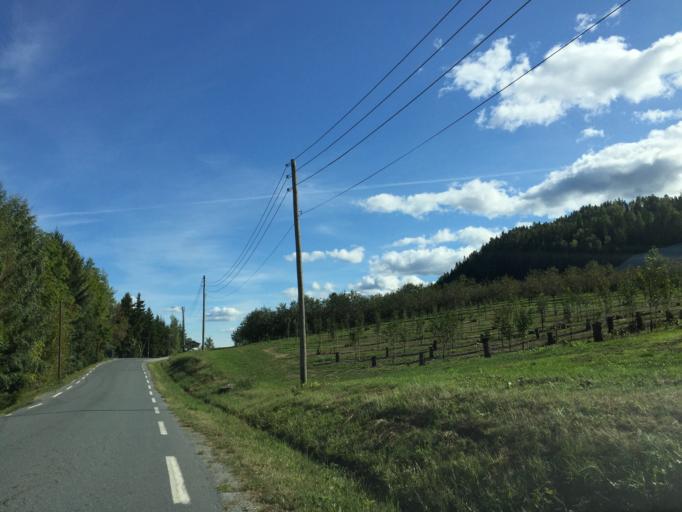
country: NO
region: Buskerud
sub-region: Ovre Eiker
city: Hokksund
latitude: 59.6862
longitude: 9.8538
